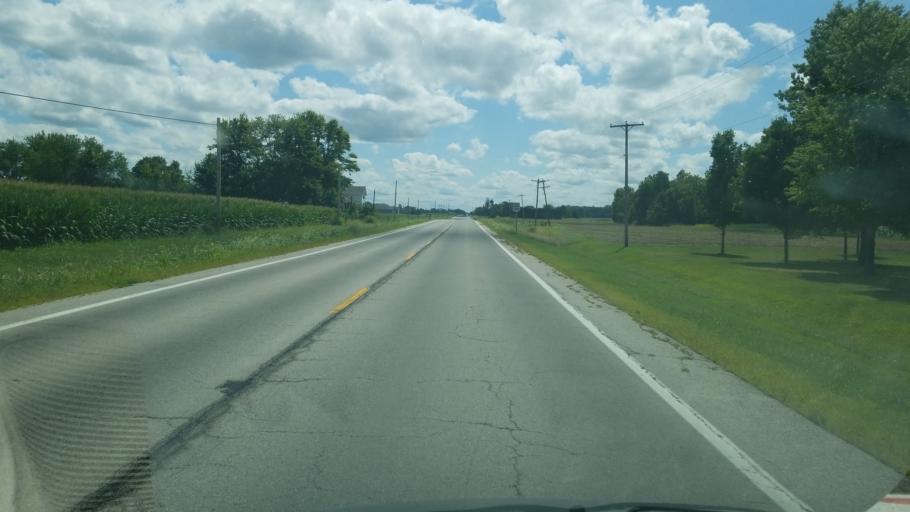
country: US
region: Ohio
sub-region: Henry County
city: Napoleon
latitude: 41.3334
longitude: -84.1189
